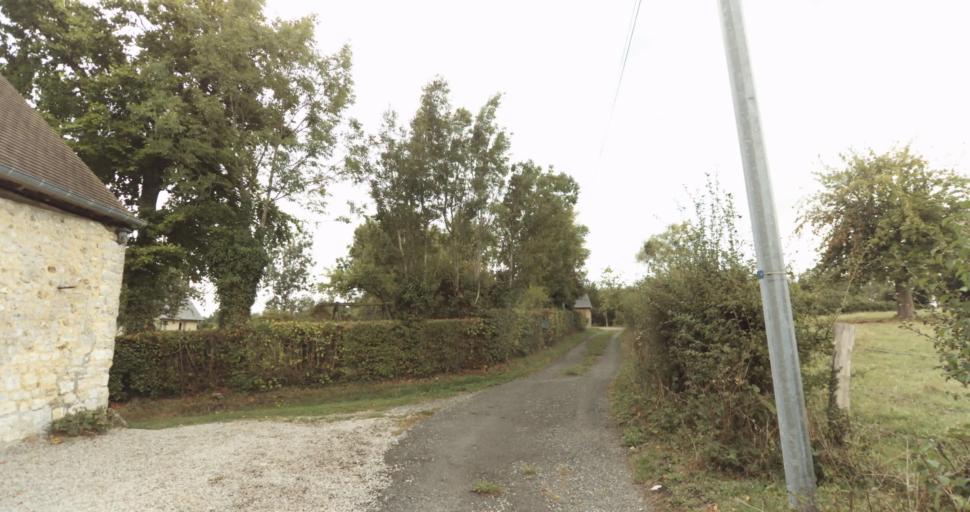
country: FR
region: Lower Normandy
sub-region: Departement de l'Orne
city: Sainte-Gauburge-Sainte-Colombe
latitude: 48.7742
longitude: 0.3781
